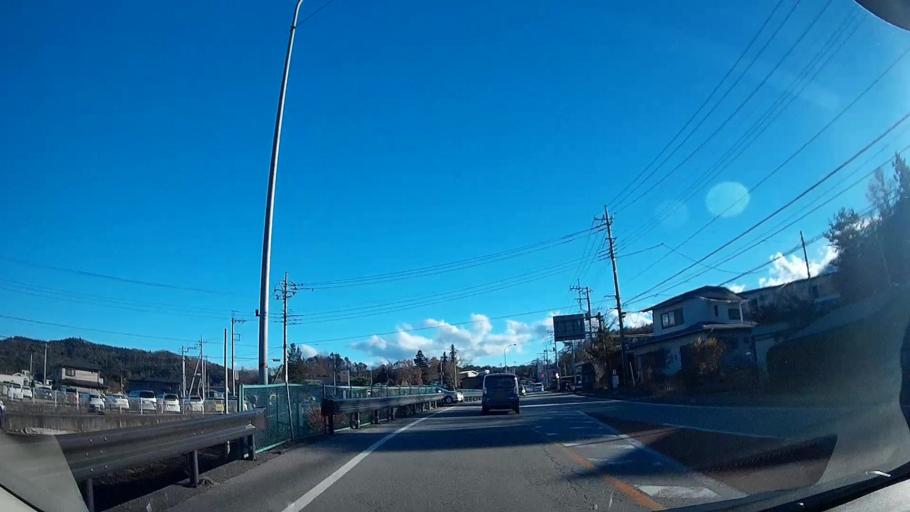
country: JP
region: Yamanashi
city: Fujikawaguchiko
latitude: 35.4631
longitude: 138.8037
